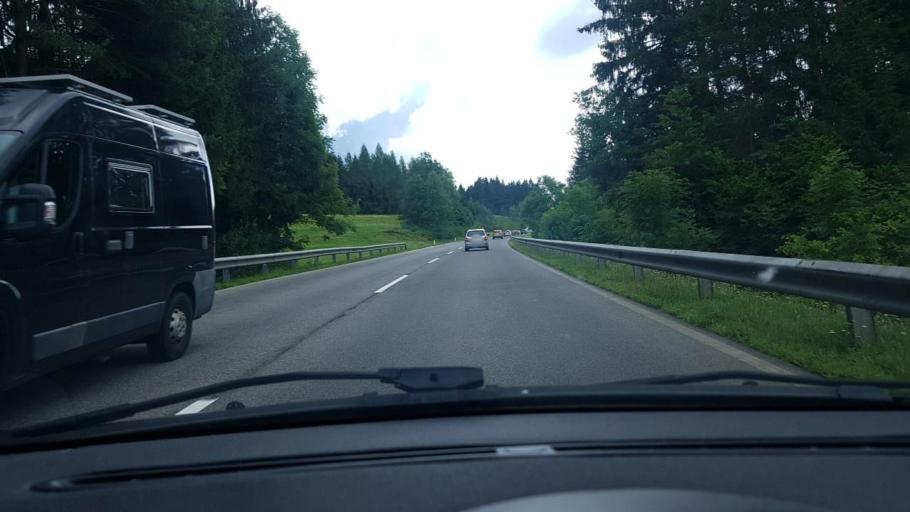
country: AT
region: Carinthia
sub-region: Politischer Bezirk Villach Land
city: Stockenboi
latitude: 46.6224
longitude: 13.4979
